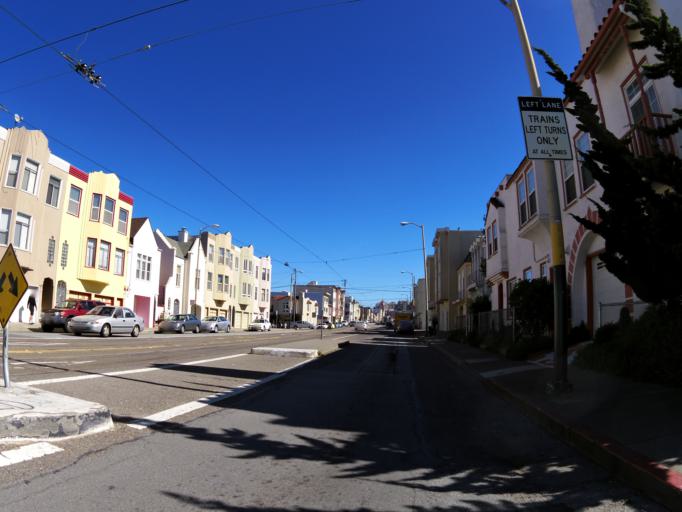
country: US
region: California
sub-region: San Mateo County
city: Daly City
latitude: 37.7616
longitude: -122.4801
